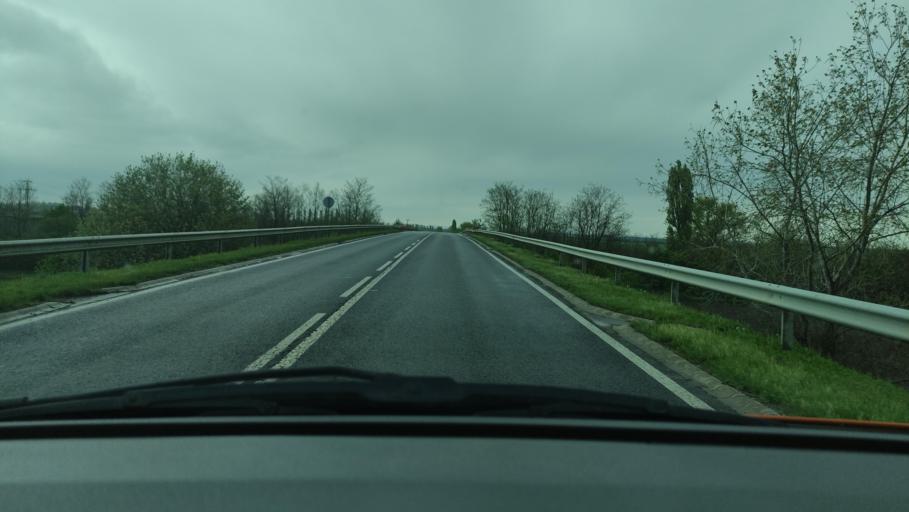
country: HU
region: Baranya
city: Mohacs
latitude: 45.9910
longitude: 18.6557
